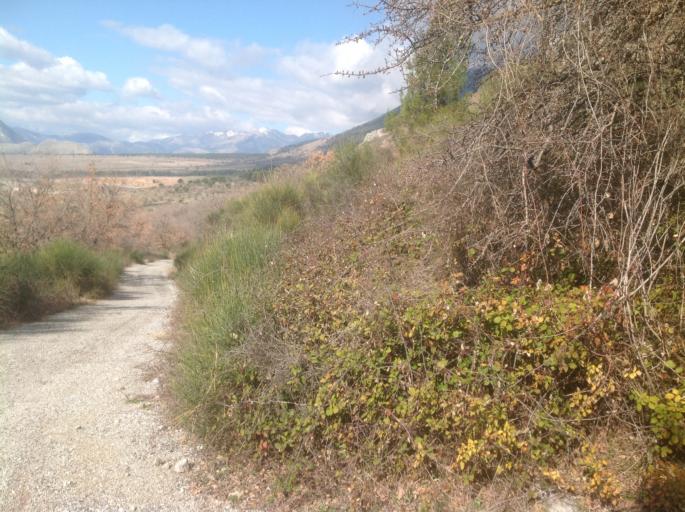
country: IT
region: Calabria
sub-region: Provincia di Cosenza
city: Frascineto
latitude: 39.8450
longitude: 16.2608
